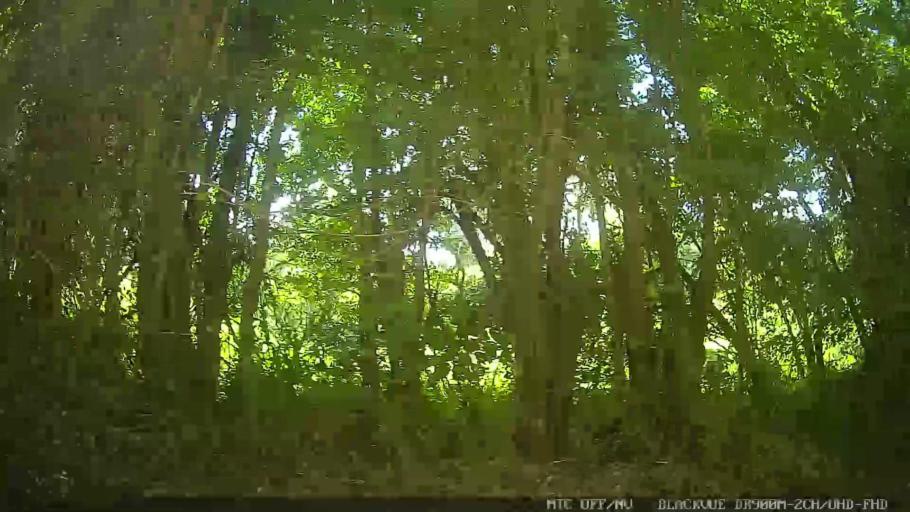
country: BR
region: Sao Paulo
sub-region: Jarinu
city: Jarinu
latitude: -23.1003
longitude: -46.6474
